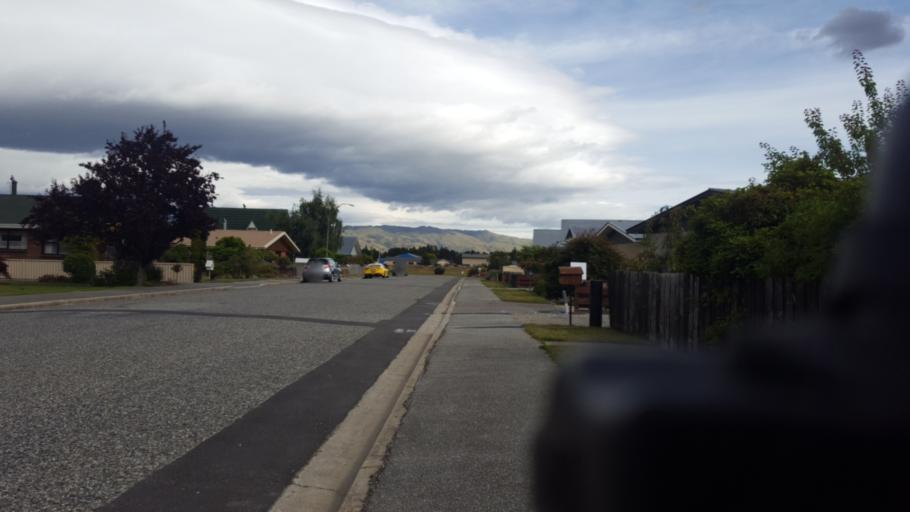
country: NZ
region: Otago
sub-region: Queenstown-Lakes District
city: Wanaka
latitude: -45.2412
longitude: 169.3920
